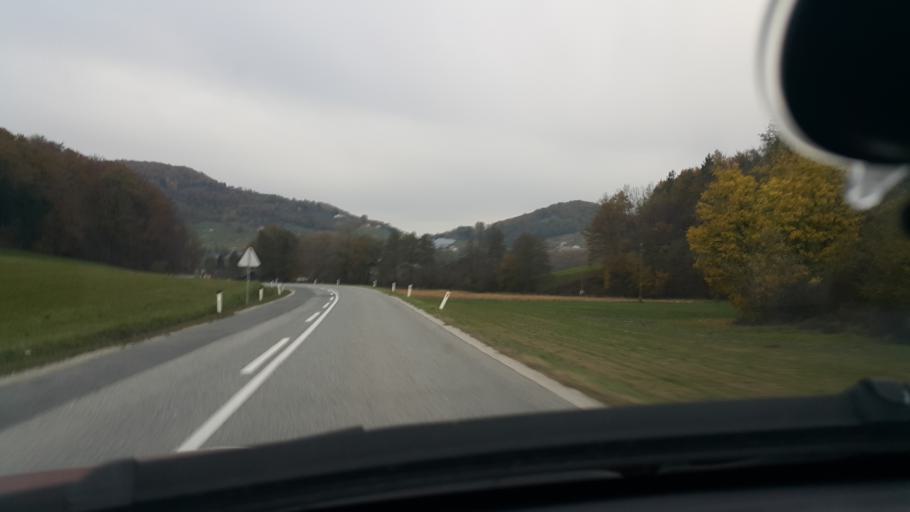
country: SI
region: Poljcane
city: Poljcane
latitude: 46.2582
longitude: 15.5679
